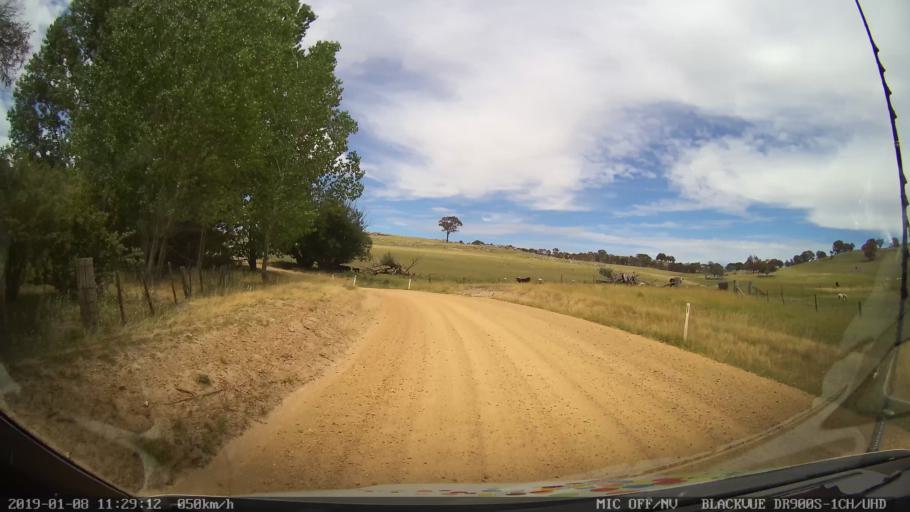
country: AU
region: New South Wales
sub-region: Guyra
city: Guyra
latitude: -30.2993
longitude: 151.5490
